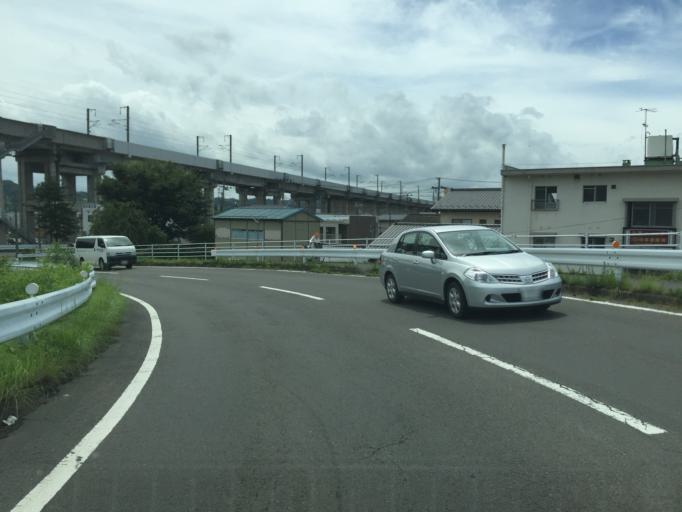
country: JP
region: Fukushima
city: Fukushima-shi
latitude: 37.7446
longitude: 140.4576
